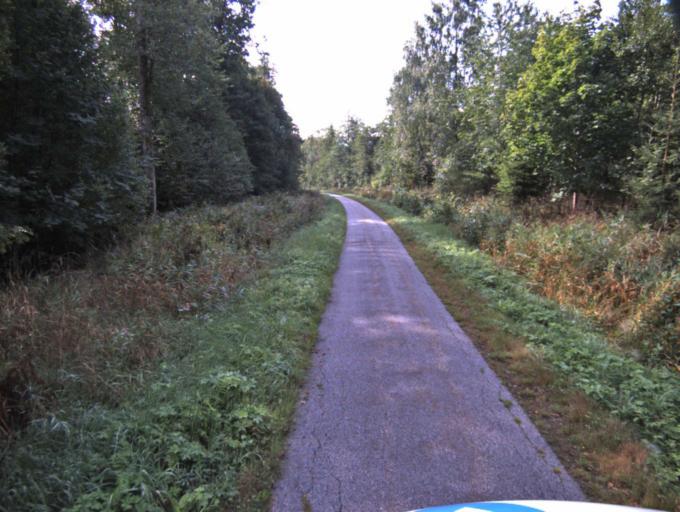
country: SE
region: Vaestra Goetaland
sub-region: Tranemo Kommun
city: Limmared
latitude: 57.6622
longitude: 13.3632
